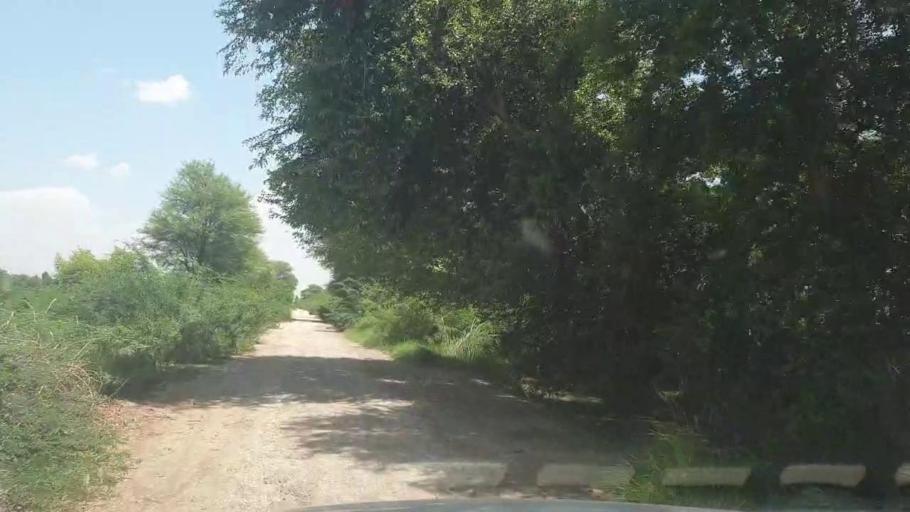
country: PK
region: Sindh
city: Kot Diji
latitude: 27.2638
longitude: 69.0185
